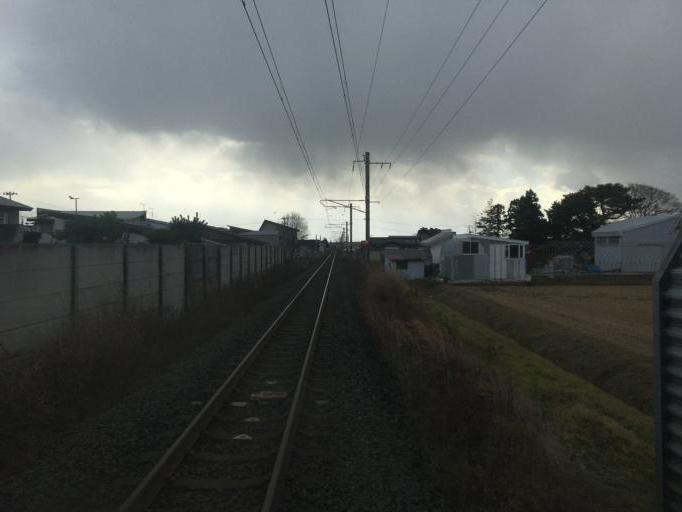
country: JP
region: Aomori
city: Aomori Shi
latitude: 40.8937
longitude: 140.6735
